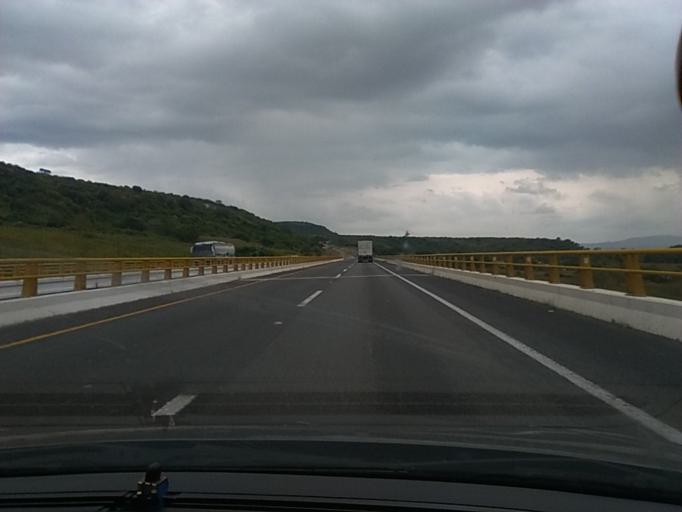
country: MX
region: Jalisco
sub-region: Zapotlan del Rey
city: Zapotlan del Rey
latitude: 20.4912
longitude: -102.9438
